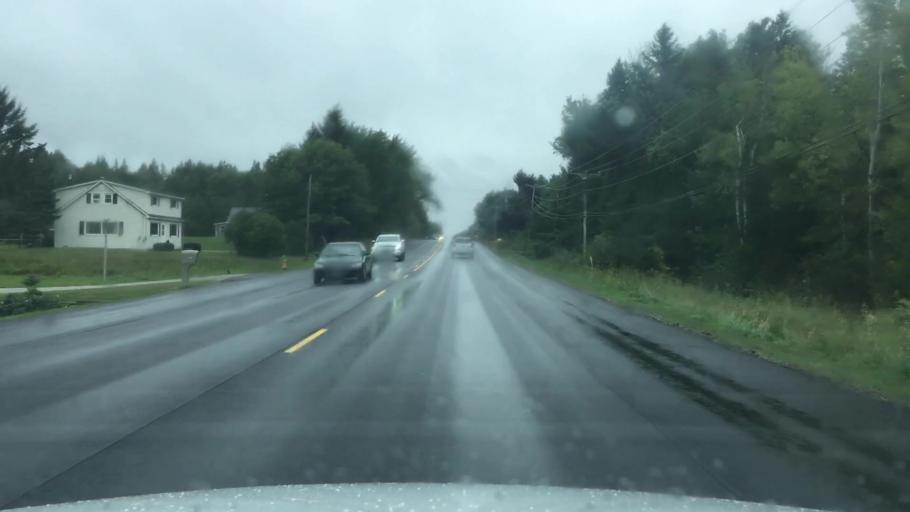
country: US
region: Maine
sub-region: Penobscot County
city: Hampden
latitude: 44.7642
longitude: -68.8516
